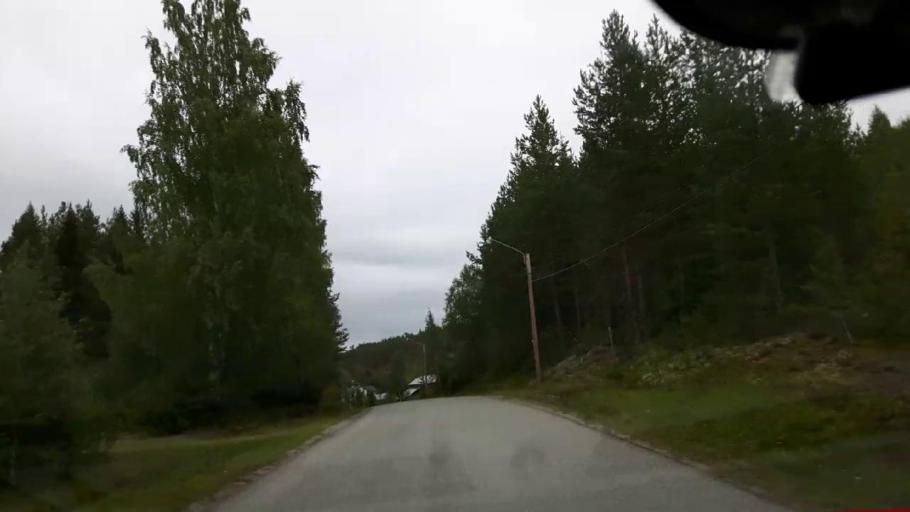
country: SE
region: Vaesternorrland
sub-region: Ange Kommun
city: Fransta
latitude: 62.7726
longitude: 15.9933
